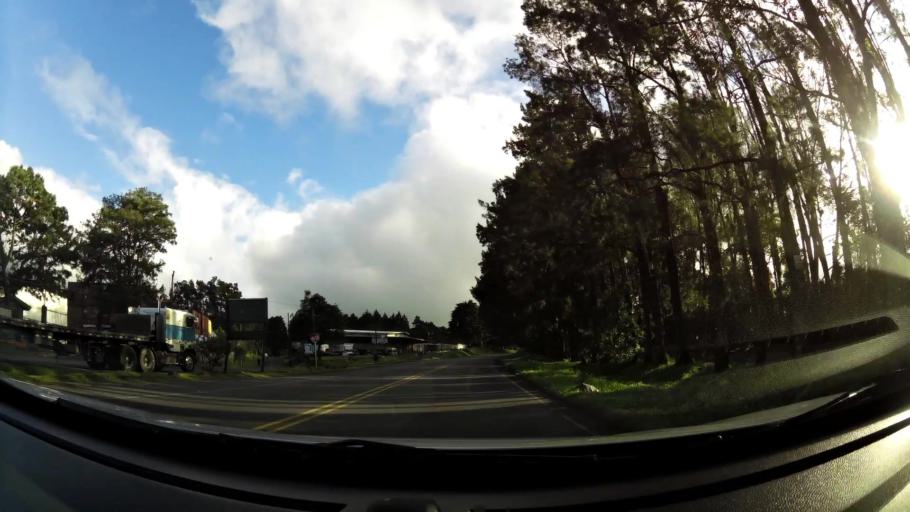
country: CR
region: Heredia
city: Angeles
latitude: 10.0277
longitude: -84.0230
